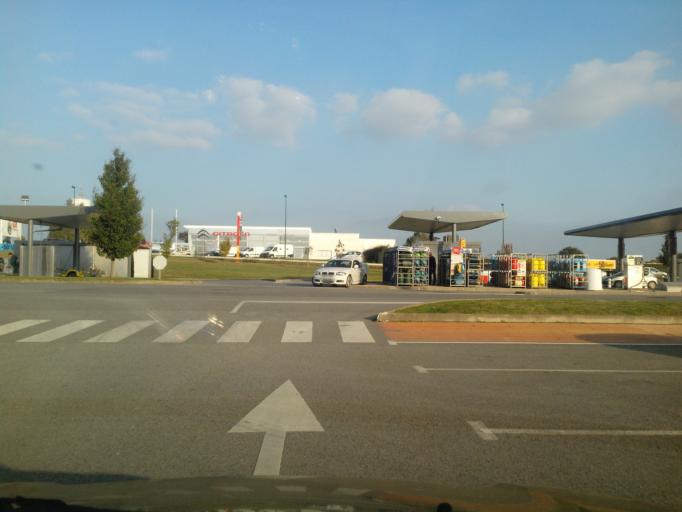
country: FR
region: Brittany
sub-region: Departement du Morbihan
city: Ploermel
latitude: 47.9317
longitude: -2.3822
